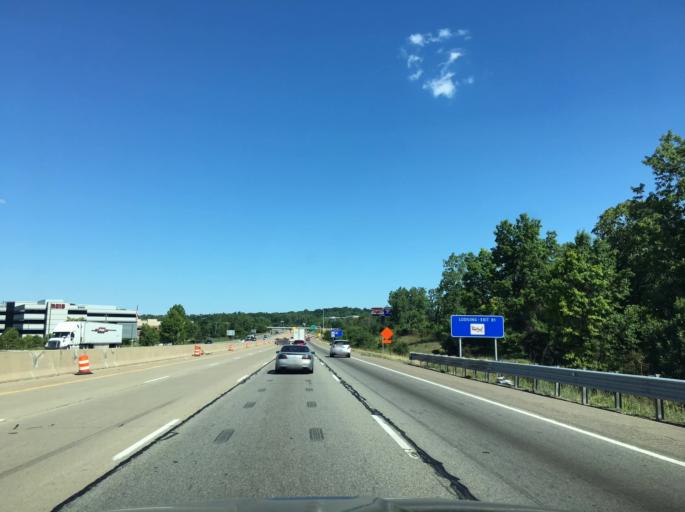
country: US
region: Michigan
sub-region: Oakland County
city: Auburn Hills
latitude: 42.6866
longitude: -83.2461
